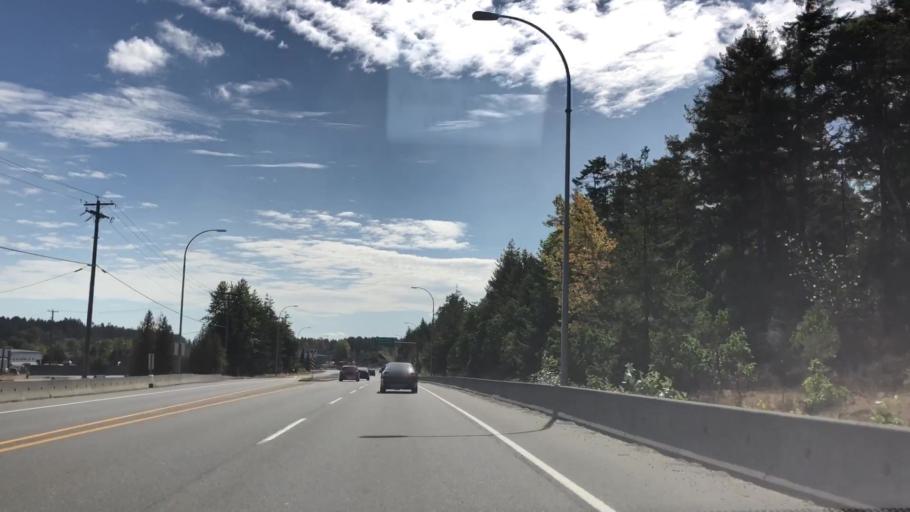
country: CA
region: British Columbia
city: Nanaimo
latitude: 49.1446
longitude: -123.8847
